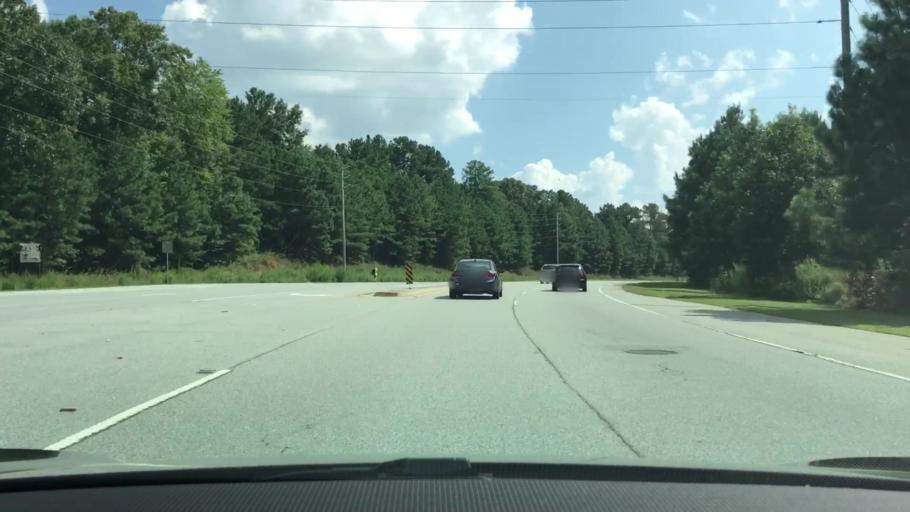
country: US
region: Georgia
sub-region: Gwinnett County
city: Sugar Hill
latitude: 34.0654
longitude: -84.0167
